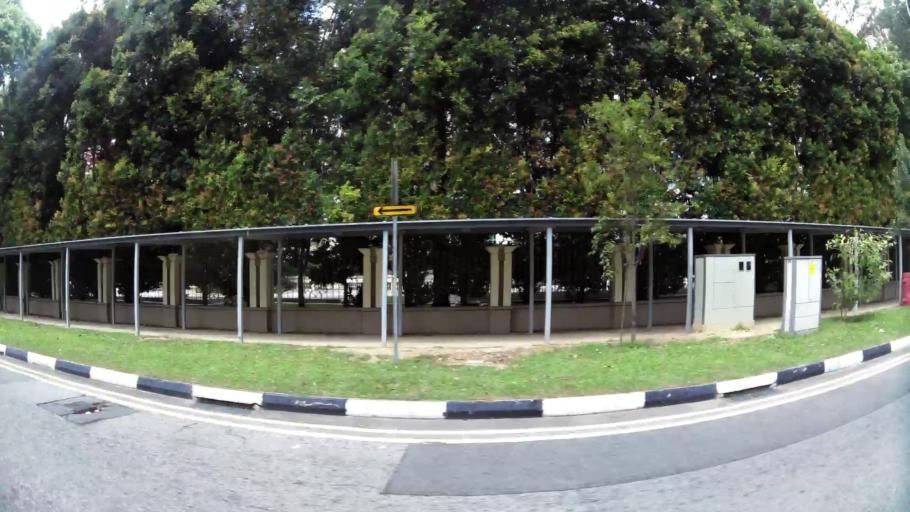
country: SG
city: Singapore
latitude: 1.2916
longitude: 103.8161
